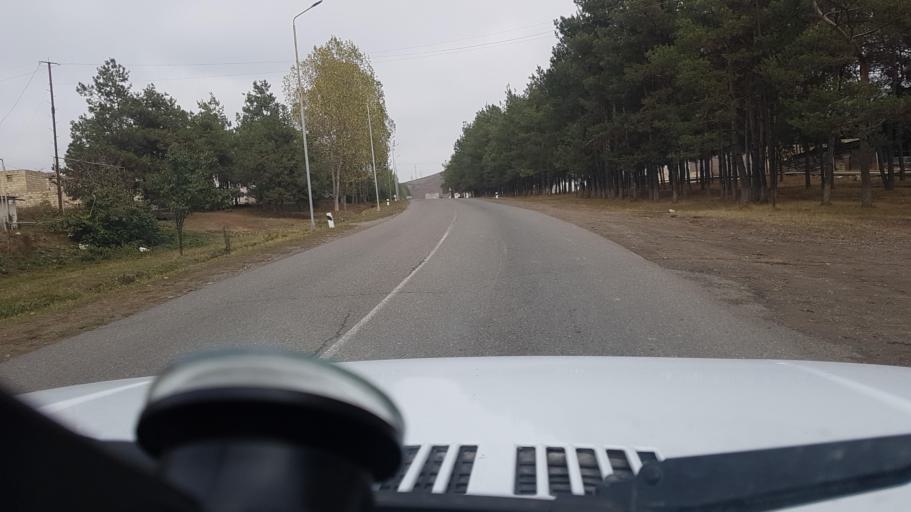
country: AZ
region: Gadabay Rayon
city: Ariqdam
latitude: 40.6040
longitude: 45.8122
